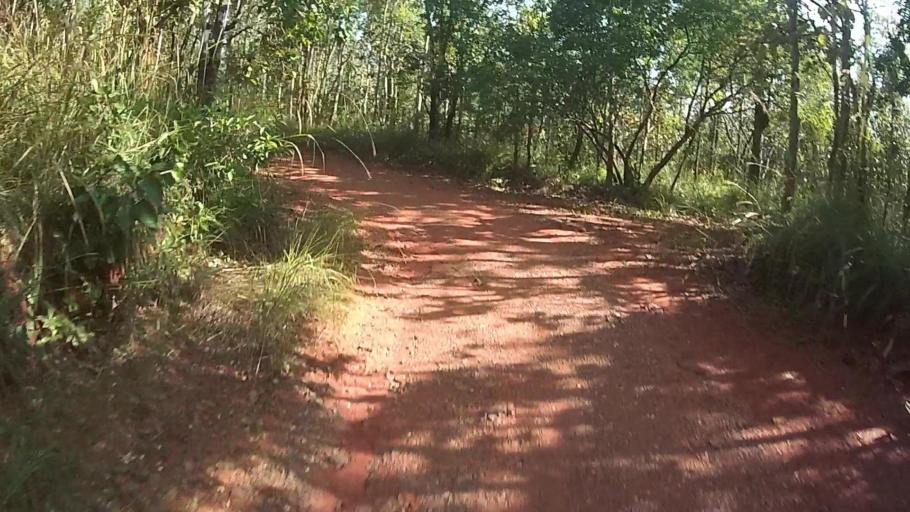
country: TH
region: Chiang Mai
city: Mae On
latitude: 18.9101
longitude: 99.2122
